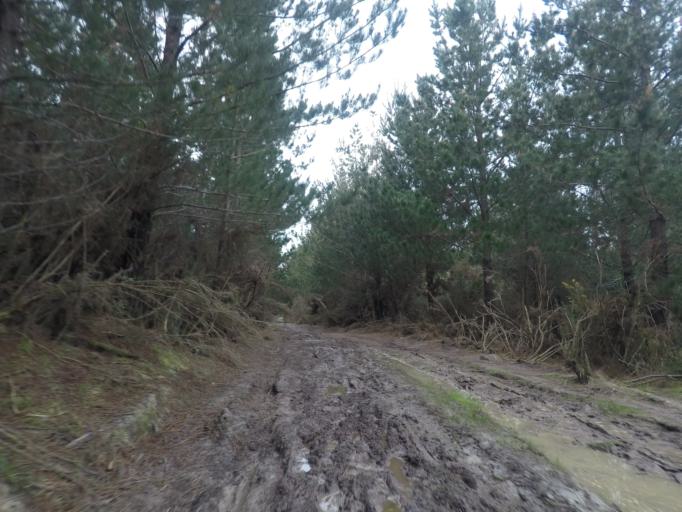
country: NZ
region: Auckland
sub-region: Auckland
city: Rothesay Bay
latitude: -36.7377
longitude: 174.5989
